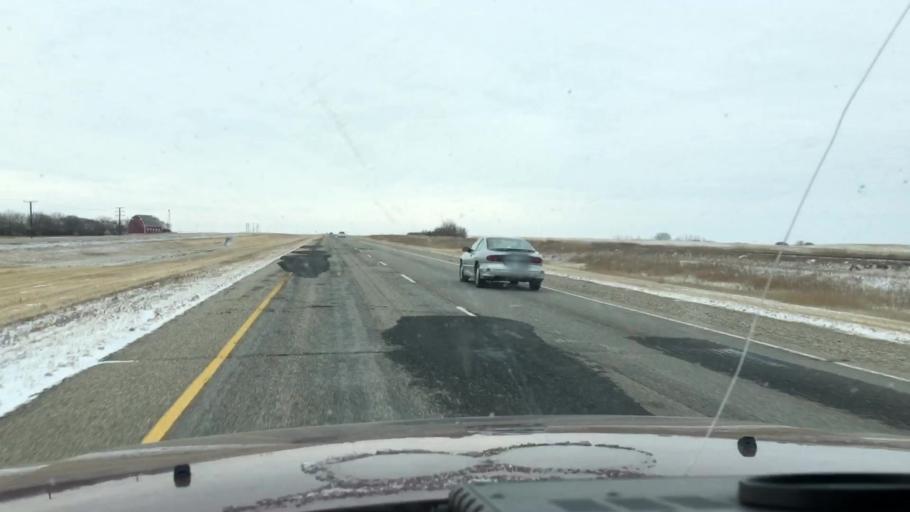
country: CA
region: Saskatchewan
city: Watrous
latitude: 51.4223
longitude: -106.1945
